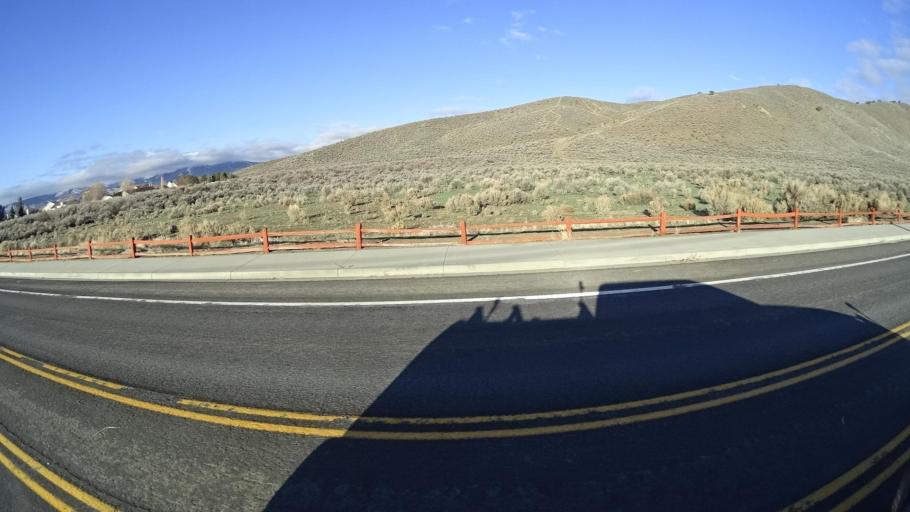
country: US
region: Nevada
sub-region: Washoe County
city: Cold Springs
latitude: 39.6840
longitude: -119.9787
